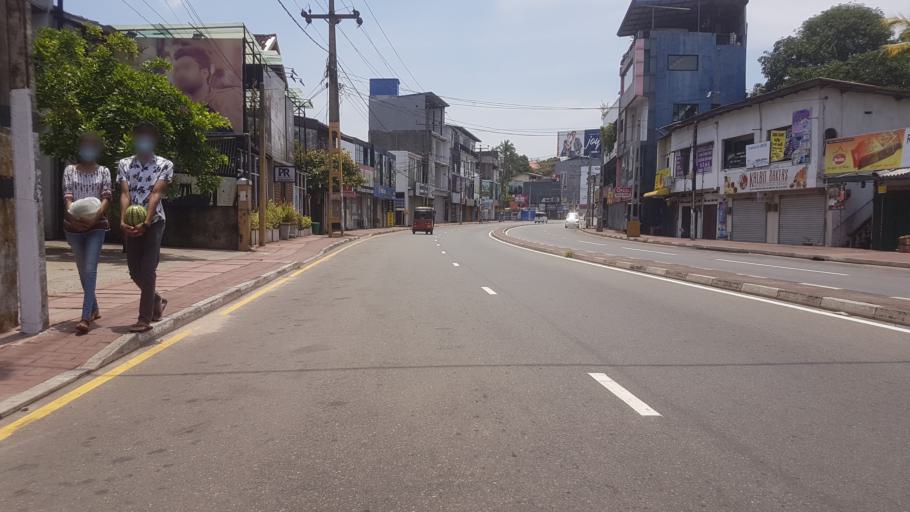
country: LK
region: Western
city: Battaramulla South
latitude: 6.8933
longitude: 79.9270
